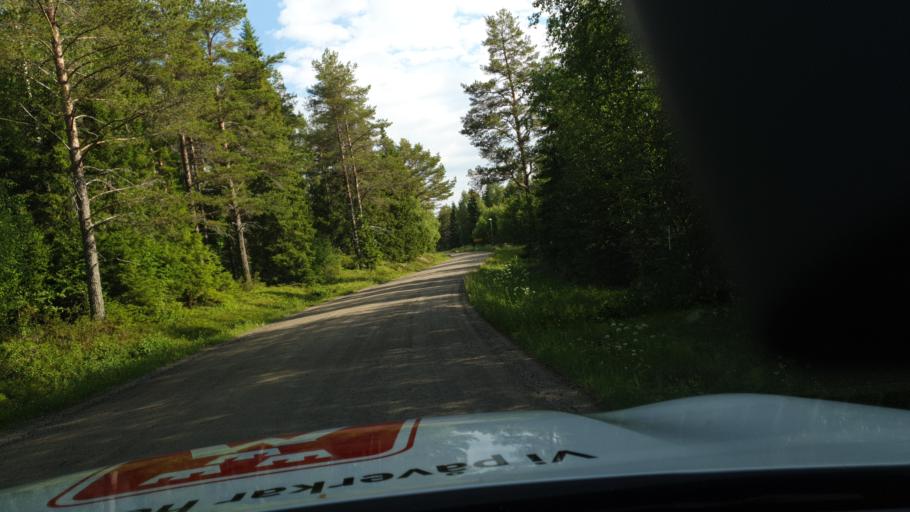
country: SE
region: Vaesterbotten
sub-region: Robertsfors Kommun
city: Robertsfors
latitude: 64.2237
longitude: 21.0696
